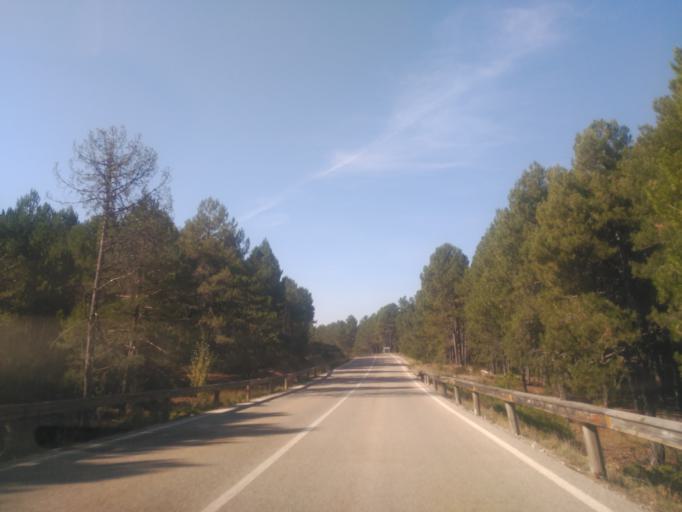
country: ES
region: Castille and Leon
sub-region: Provincia de Soria
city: Herrera de Soria
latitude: 41.7591
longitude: -3.0368
